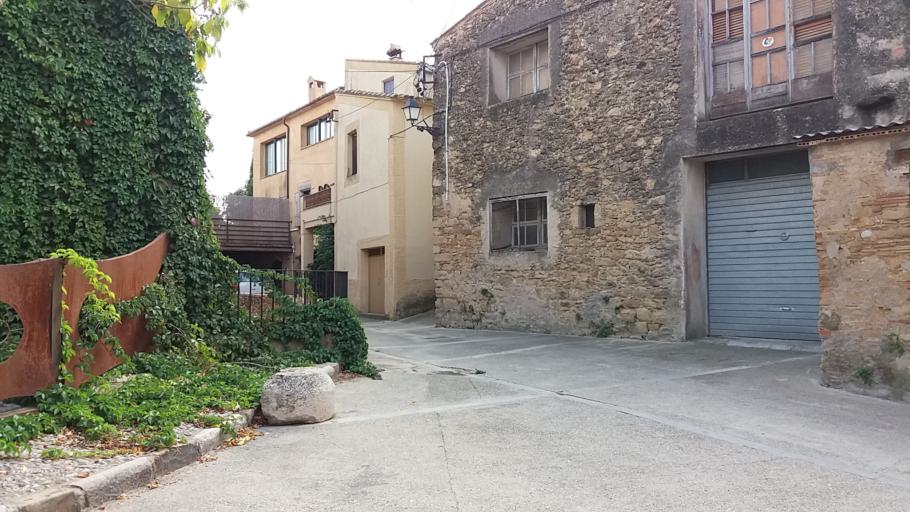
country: ES
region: Catalonia
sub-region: Provincia de Girona
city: Vilademuls
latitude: 42.1247
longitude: 2.9067
